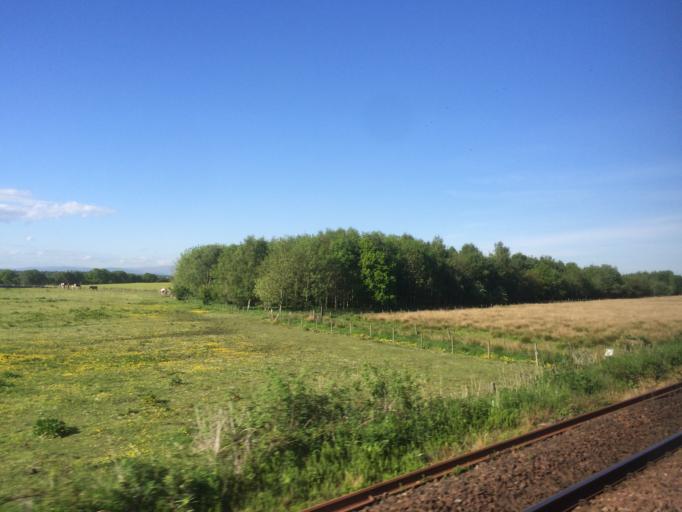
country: GB
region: Scotland
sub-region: Falkirk
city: Bonnybridge
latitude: 55.9877
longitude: -3.9048
